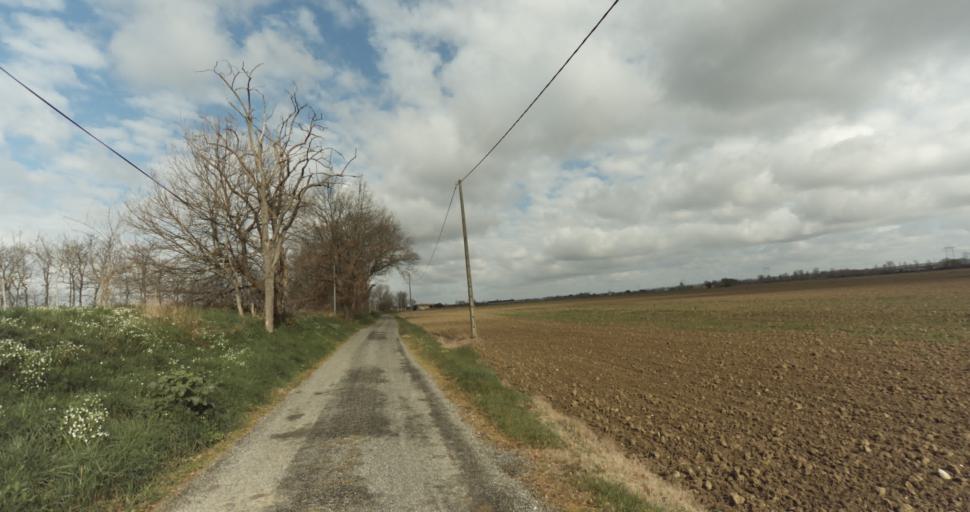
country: FR
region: Midi-Pyrenees
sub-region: Departement de la Haute-Garonne
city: Auterive
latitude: 43.3467
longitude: 1.4441
